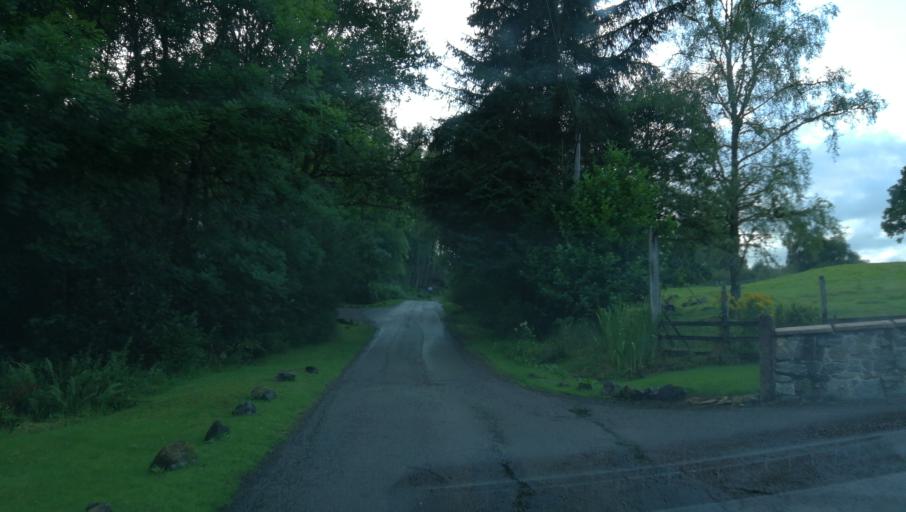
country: GB
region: Scotland
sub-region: Highland
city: Spean Bridge
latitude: 57.0688
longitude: -4.8228
